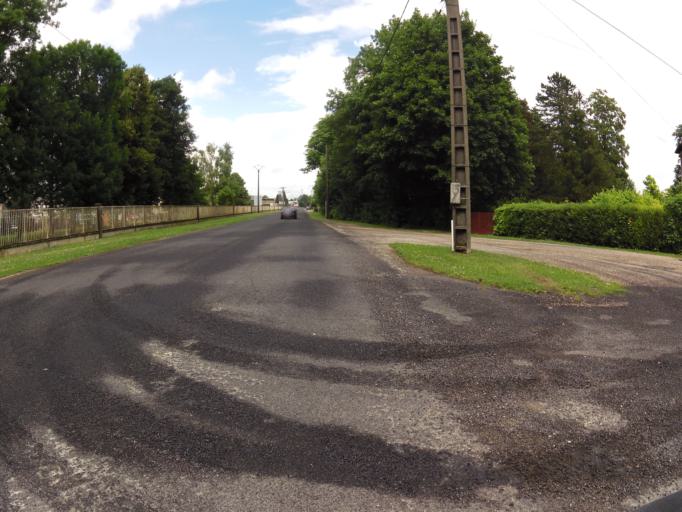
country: FR
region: Lorraine
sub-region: Departement de la Meuse
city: Revigny-sur-Ornain
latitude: 48.8169
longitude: 4.9776
